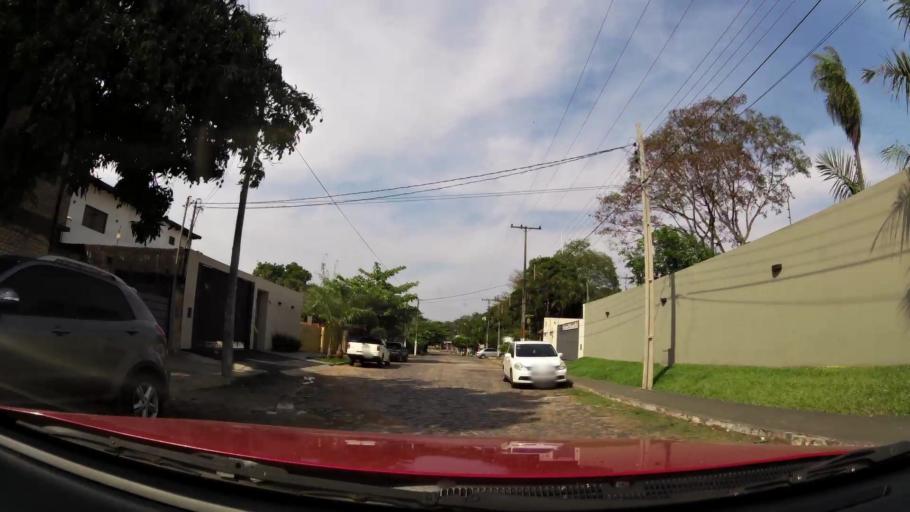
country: PY
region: Central
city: Fernando de la Mora
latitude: -25.2619
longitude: -57.5520
